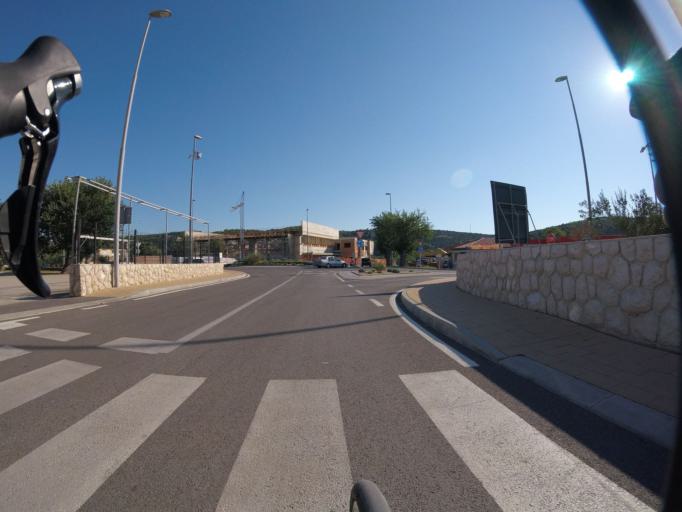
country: HR
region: Primorsko-Goranska
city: Lopar
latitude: 44.8302
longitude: 14.7314
